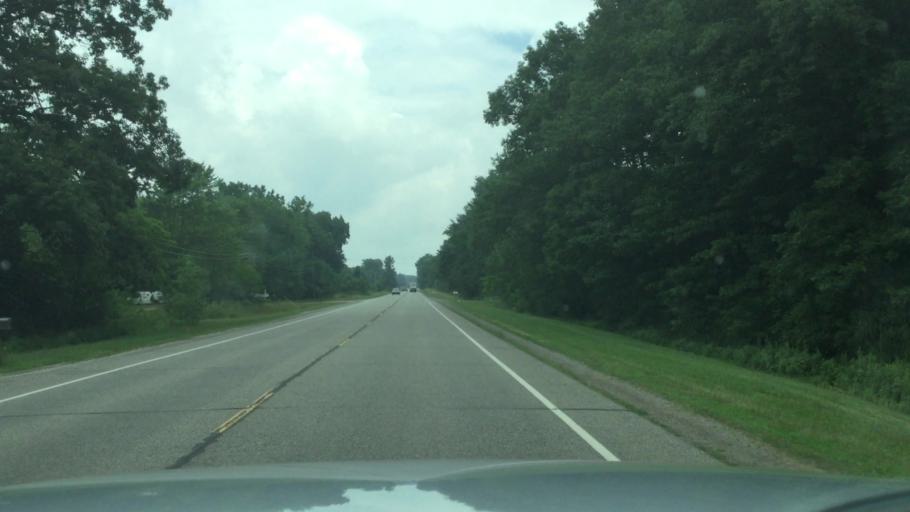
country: US
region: Michigan
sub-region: Shiawassee County
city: Durand
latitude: 42.9433
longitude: -83.9365
